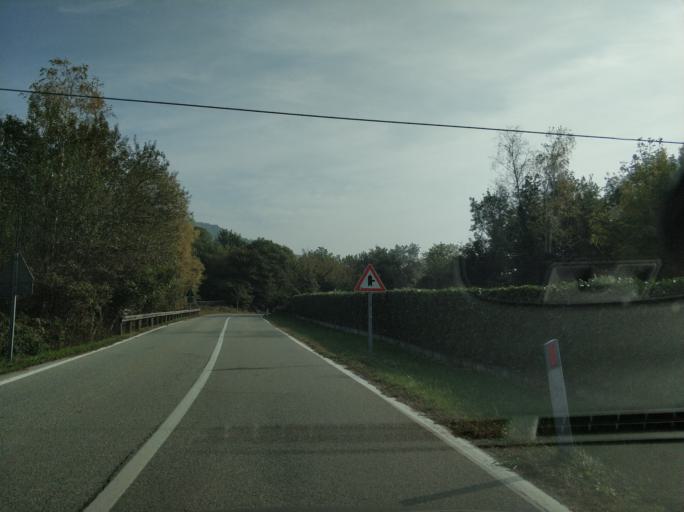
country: IT
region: Piedmont
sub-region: Provincia di Torino
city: Chiaverano
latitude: 45.5075
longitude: 7.9014
